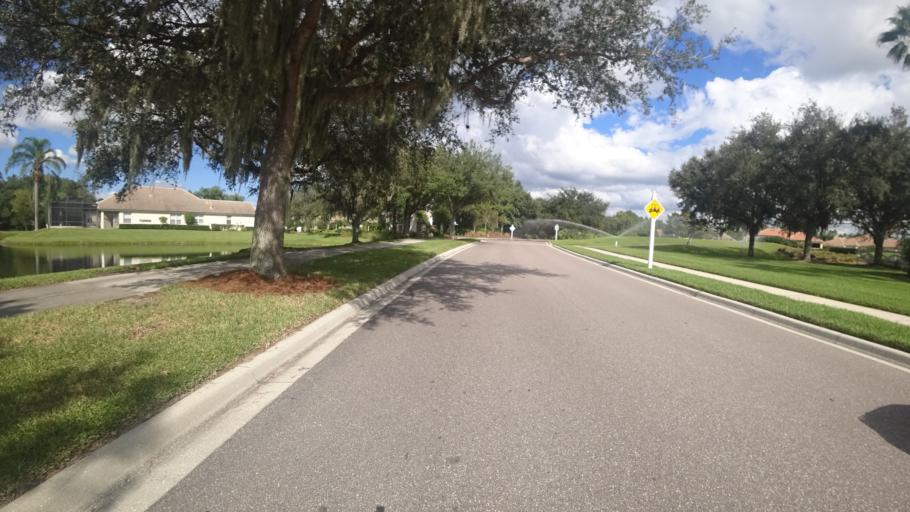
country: US
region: Florida
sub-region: Sarasota County
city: The Meadows
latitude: 27.3987
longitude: -82.4176
